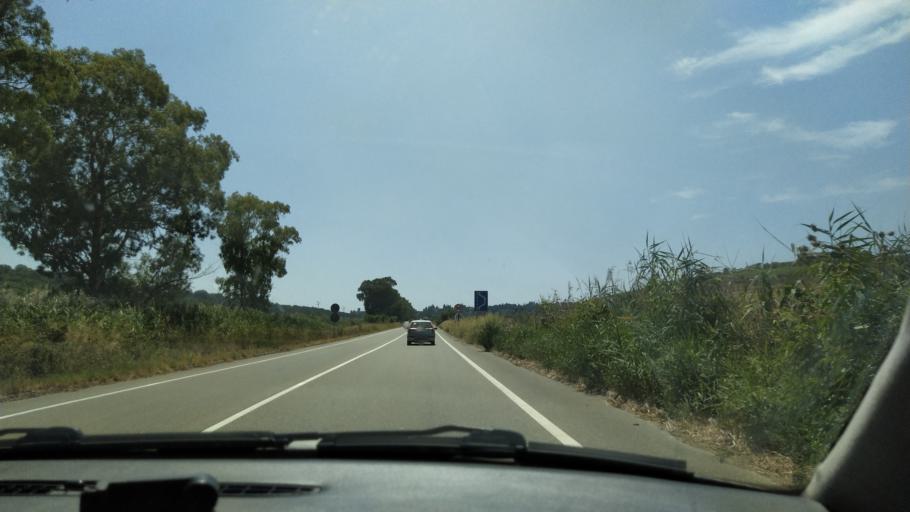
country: IT
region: Basilicate
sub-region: Provincia di Matera
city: Bernalda
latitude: 40.4421
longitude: 16.7822
